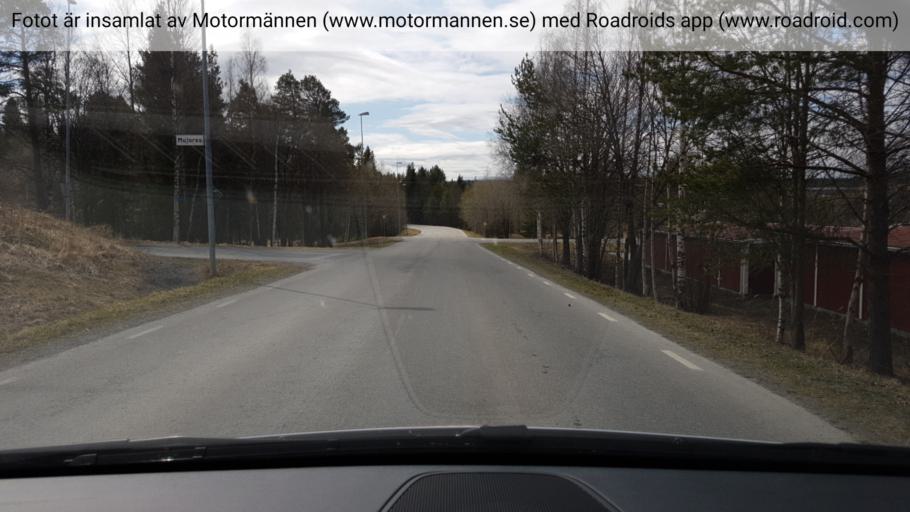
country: SE
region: Jaemtland
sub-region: OEstersunds Kommun
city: Brunflo
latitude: 63.0735
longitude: 14.8190
